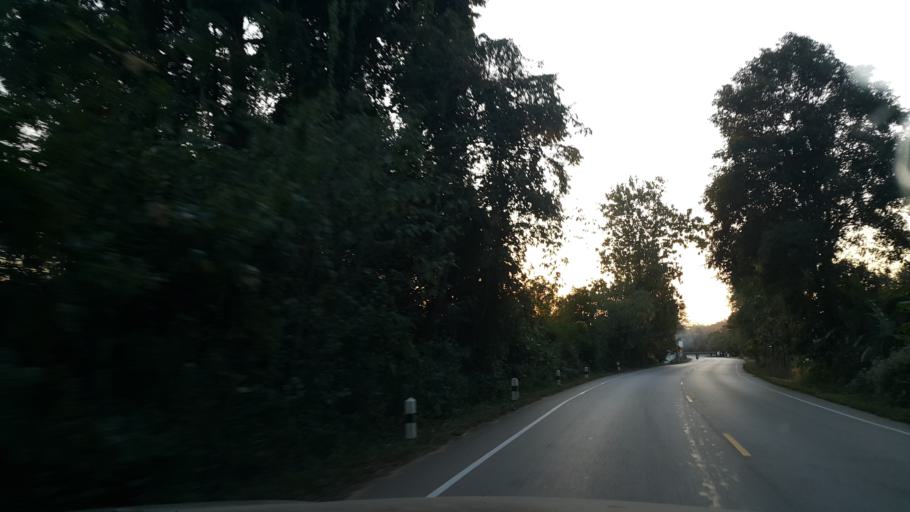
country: TH
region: Phrae
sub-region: Amphoe Wang Chin
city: Wang Chin
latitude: 17.8461
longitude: 99.6332
